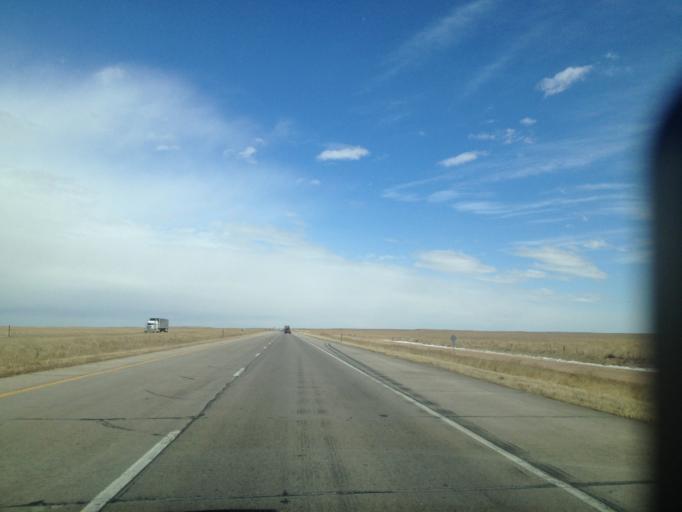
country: US
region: Colorado
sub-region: Weld County
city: Keenesburg
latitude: 40.1739
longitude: -104.3346
